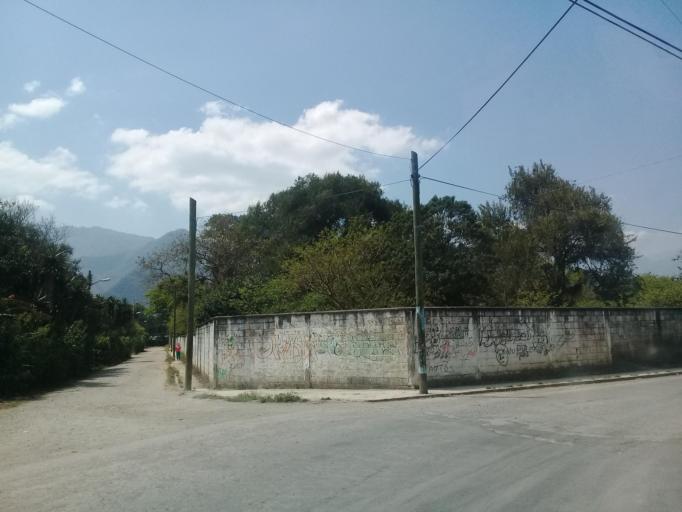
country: MX
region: Veracruz
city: Jalapilla
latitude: 18.8146
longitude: -97.0644
